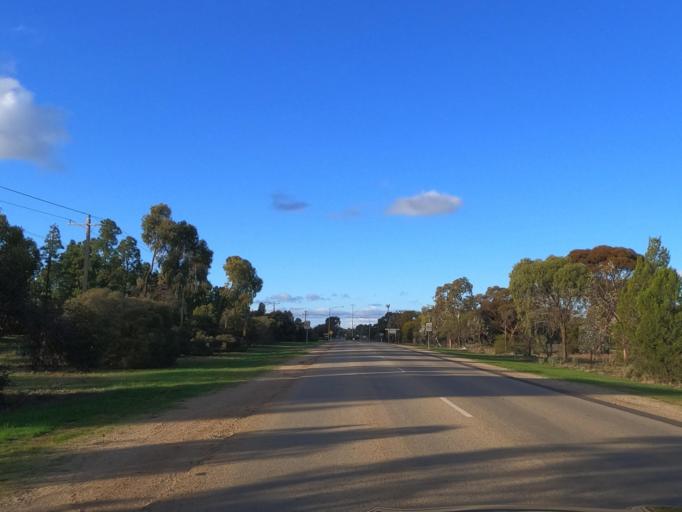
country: AU
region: Victoria
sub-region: Swan Hill
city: Swan Hill
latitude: -35.3439
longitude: 143.5287
